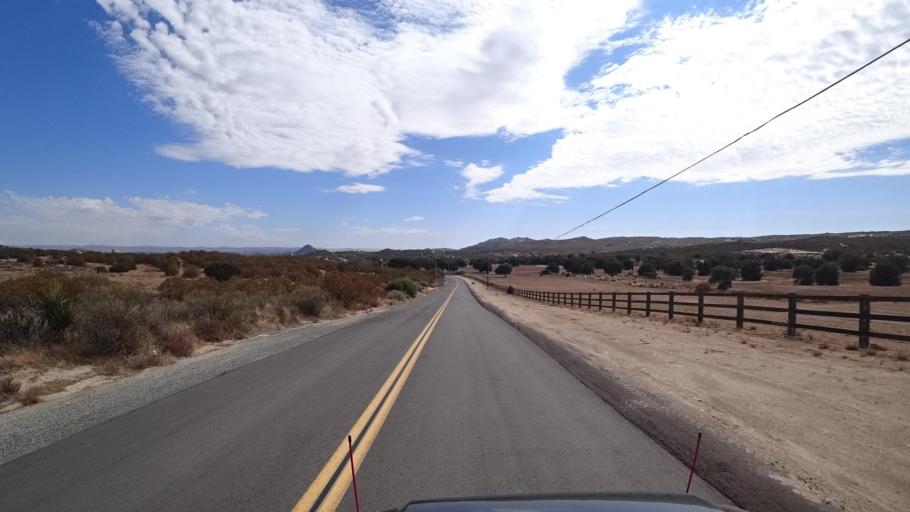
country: MX
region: Baja California
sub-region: Tecate
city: Cereso del Hongo
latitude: 32.6531
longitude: -116.2908
